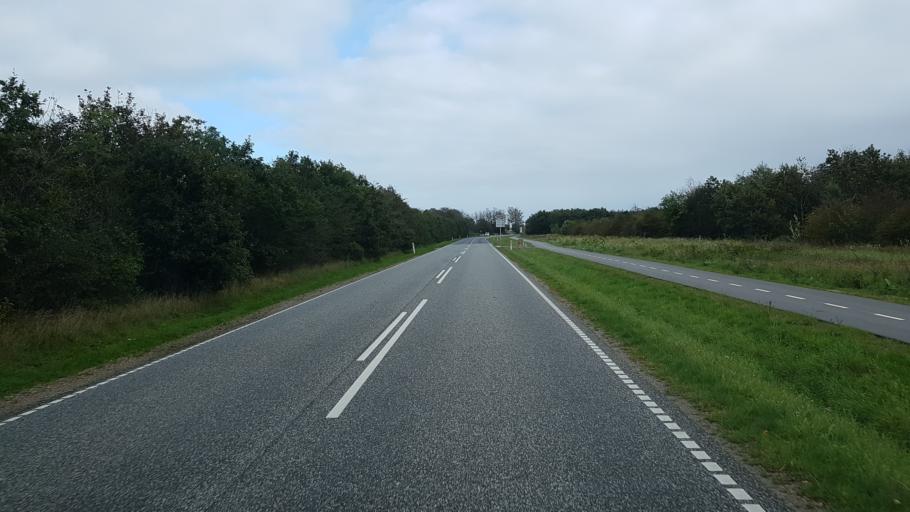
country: DK
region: South Denmark
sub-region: Billund Kommune
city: Grindsted
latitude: 55.7647
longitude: 8.8653
